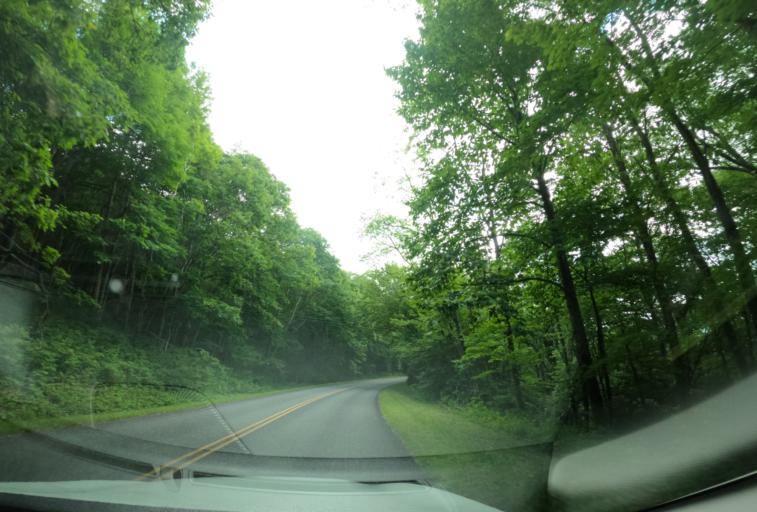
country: US
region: North Carolina
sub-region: Haywood County
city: Hazelwood
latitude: 35.4247
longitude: -83.0471
